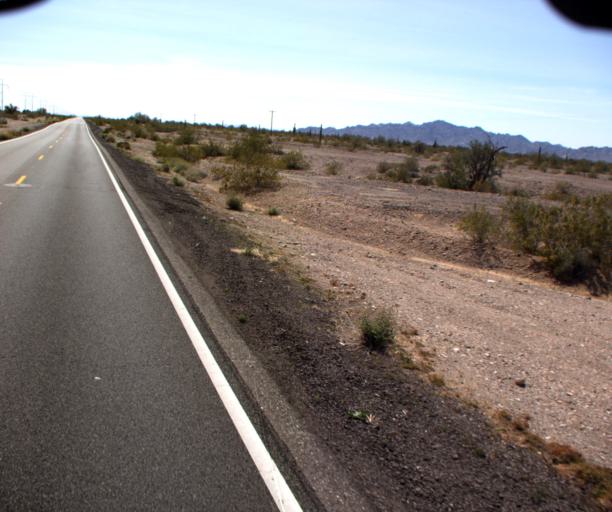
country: US
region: Arizona
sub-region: La Paz County
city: Quartzsite
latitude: 33.6098
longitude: -114.2171
